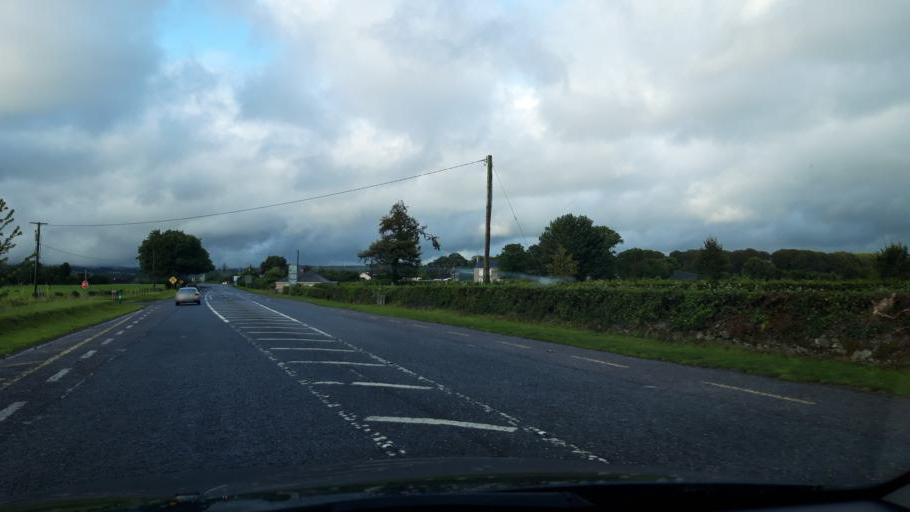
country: IE
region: Munster
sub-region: County Cork
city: Fermoy
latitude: 52.1591
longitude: -8.2723
